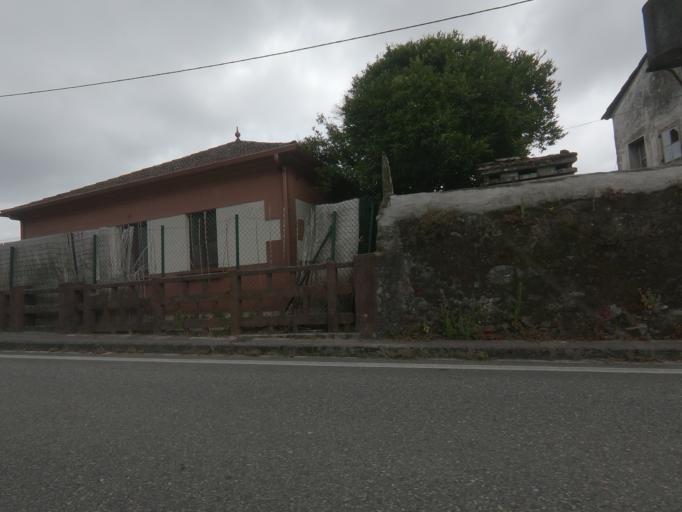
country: ES
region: Galicia
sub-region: Provincia de Pontevedra
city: O Rosal
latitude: 41.9304
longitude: -8.8024
